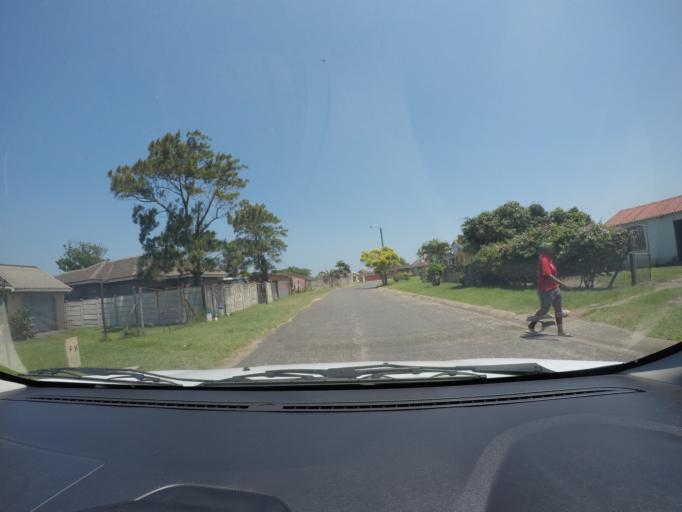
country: ZA
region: KwaZulu-Natal
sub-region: uThungulu District Municipality
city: eSikhawini
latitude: -28.8707
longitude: 31.9053
